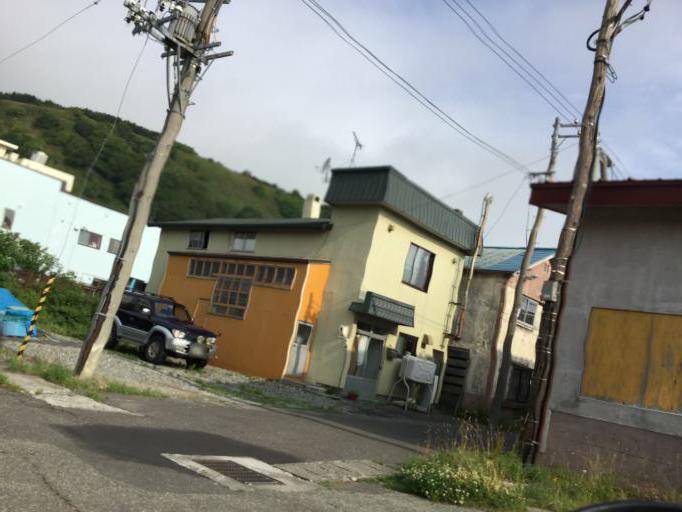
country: JP
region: Hokkaido
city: Wakkanai
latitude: 45.4057
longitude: 141.6753
